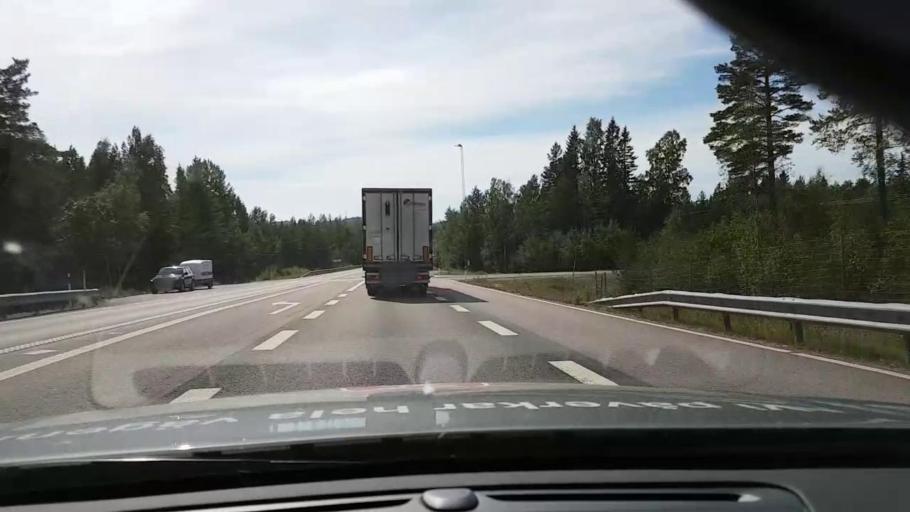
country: SE
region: Vaesternorrland
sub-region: OErnskoeldsviks Kommun
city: Husum
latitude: 63.4643
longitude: 19.2664
